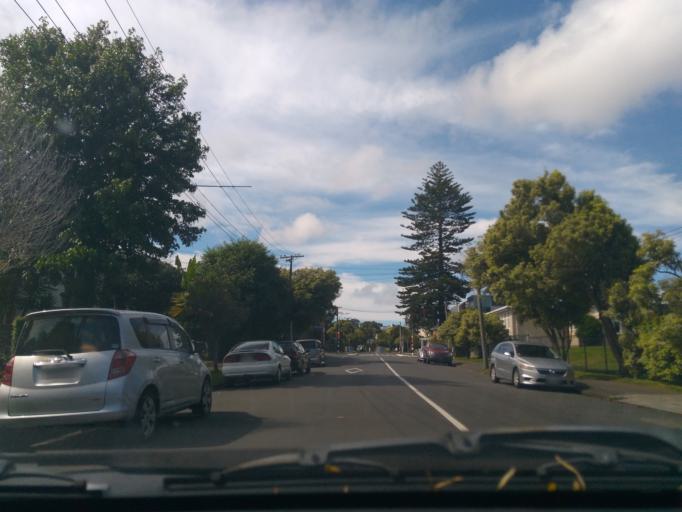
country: NZ
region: Auckland
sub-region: Auckland
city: Auckland
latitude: -36.8808
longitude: 174.7265
